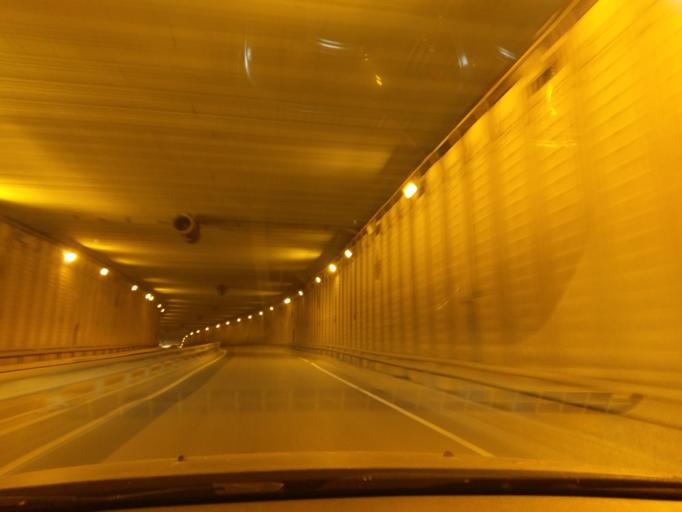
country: TR
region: Istanbul
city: Bahcelievler
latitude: 41.0143
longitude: 28.8430
